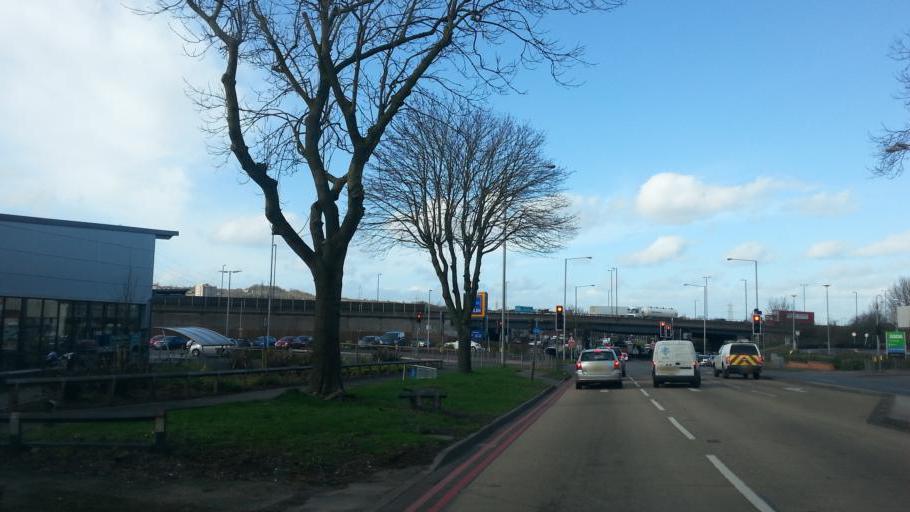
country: GB
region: England
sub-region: Sandwell
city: Oldbury
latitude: 52.4893
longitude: -2.0195
